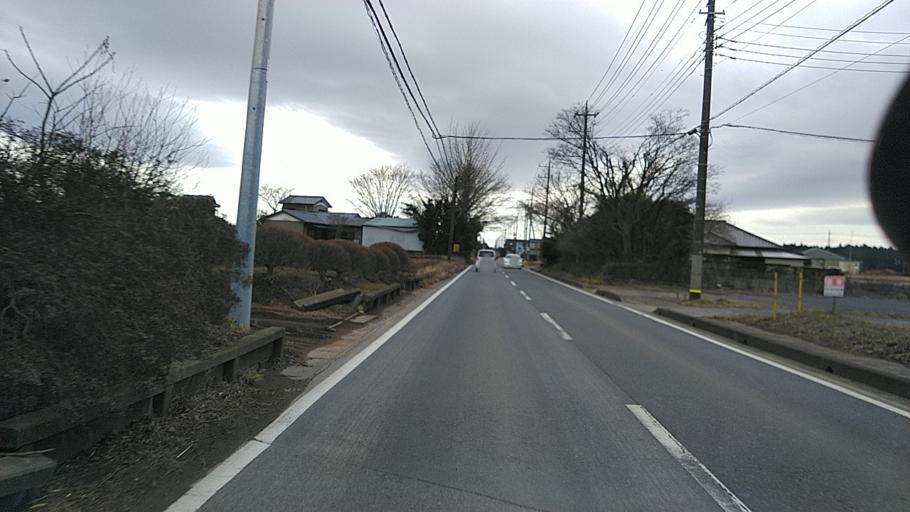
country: JP
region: Chiba
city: Sawara
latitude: 35.8374
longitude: 140.4558
